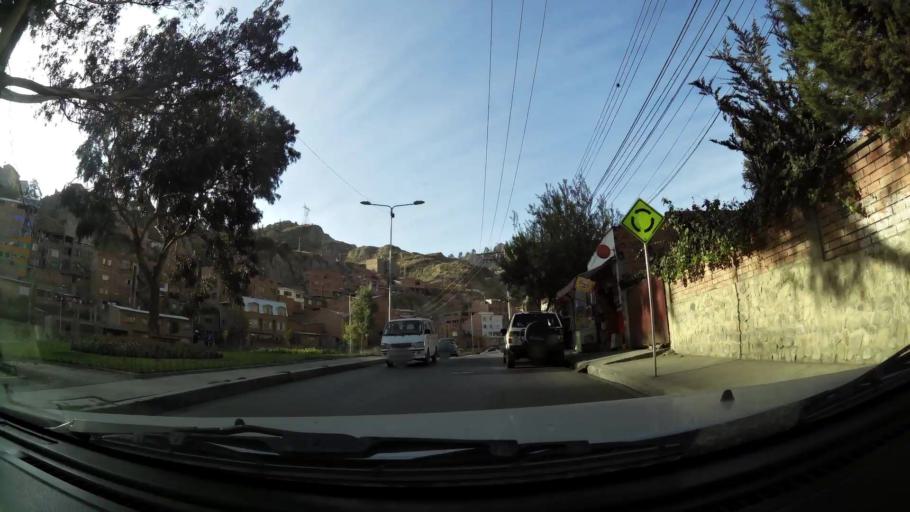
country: BO
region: La Paz
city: La Paz
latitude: -16.5251
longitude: -68.0997
